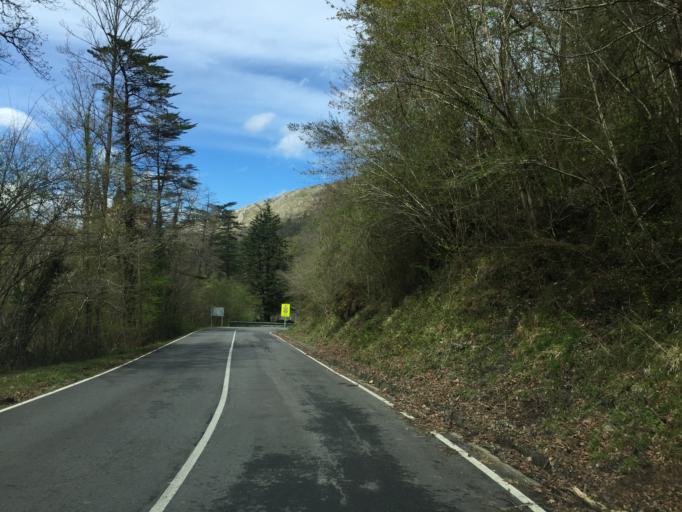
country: ES
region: Asturias
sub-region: Province of Asturias
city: Amieva
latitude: 43.3064
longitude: -5.0498
